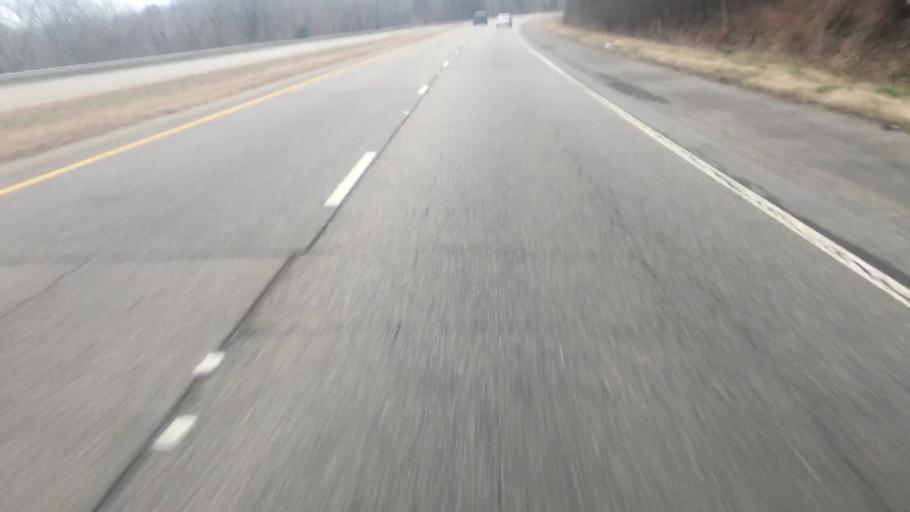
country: US
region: Alabama
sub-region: Walker County
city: Cordova
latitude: 33.8161
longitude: -87.1495
